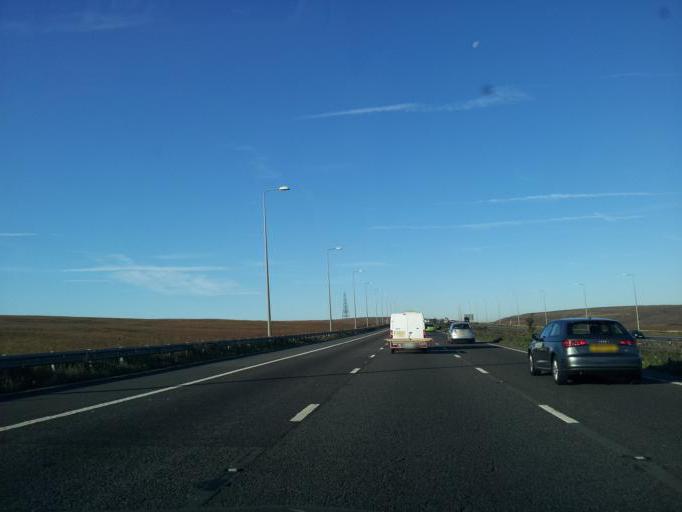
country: GB
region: England
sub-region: Borough of Oldham
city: Diggle
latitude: 53.6317
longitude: -2.0032
